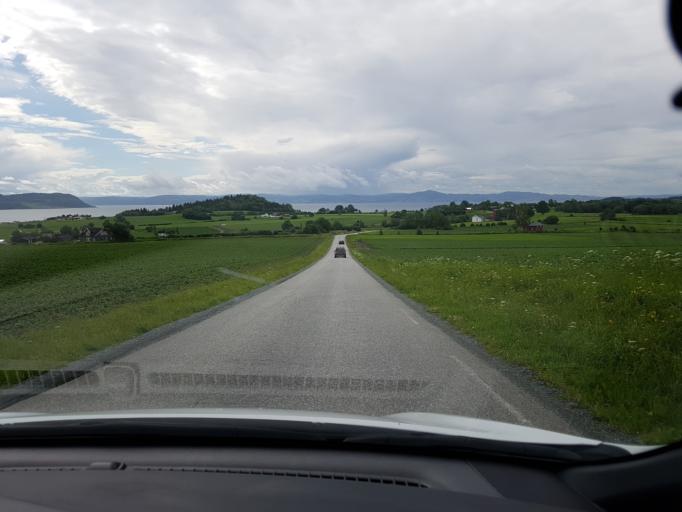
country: NO
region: Nord-Trondelag
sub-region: Frosta
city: Frosta
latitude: 63.5772
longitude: 10.7127
